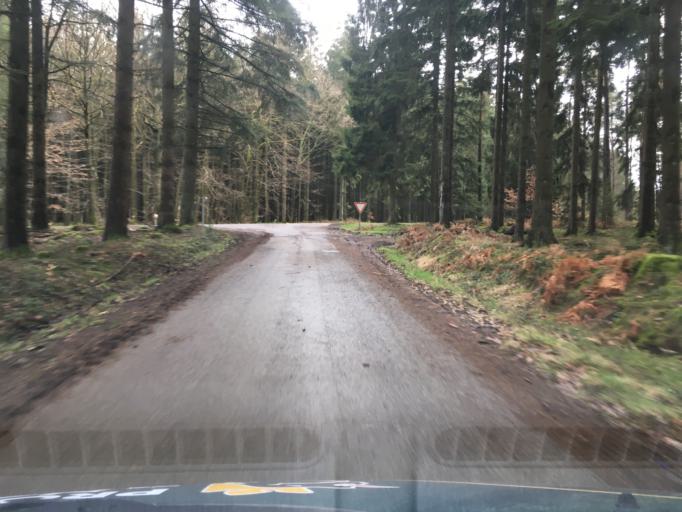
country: FR
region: Champagne-Ardenne
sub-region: Departement des Ardennes
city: Haybes
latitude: 50.0436
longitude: 4.6728
